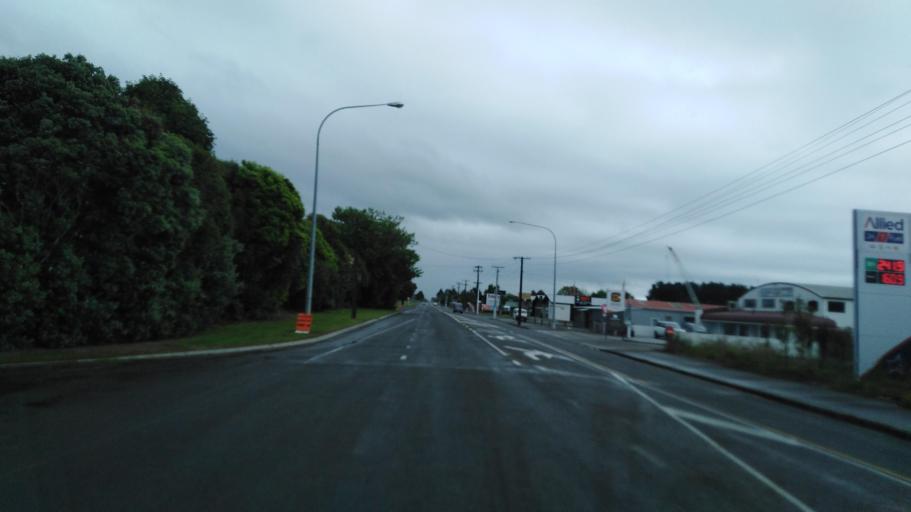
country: NZ
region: Manawatu-Wanganui
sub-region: Horowhenua District
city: Levin
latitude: -40.6365
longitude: 175.2724
